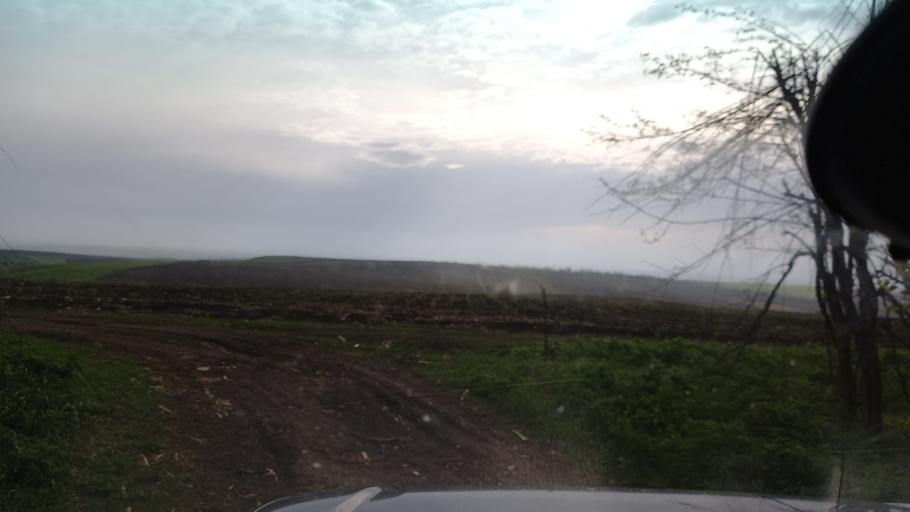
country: RU
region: Kabardino-Balkariya
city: Kuba-Taba
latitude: 43.8145
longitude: 43.4100
